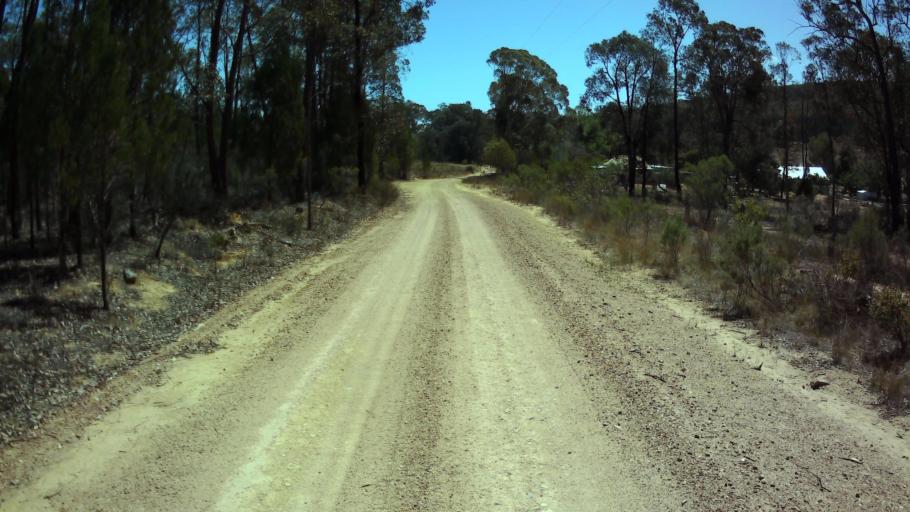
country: AU
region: New South Wales
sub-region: Cowra
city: Cowra
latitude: -33.8399
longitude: 148.4519
